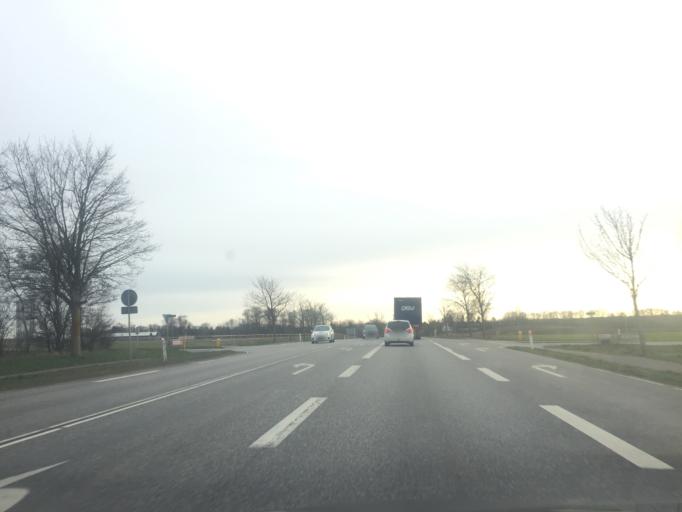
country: DK
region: Zealand
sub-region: Lejre Kommune
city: Lejre
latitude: 55.5930
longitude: 12.0117
